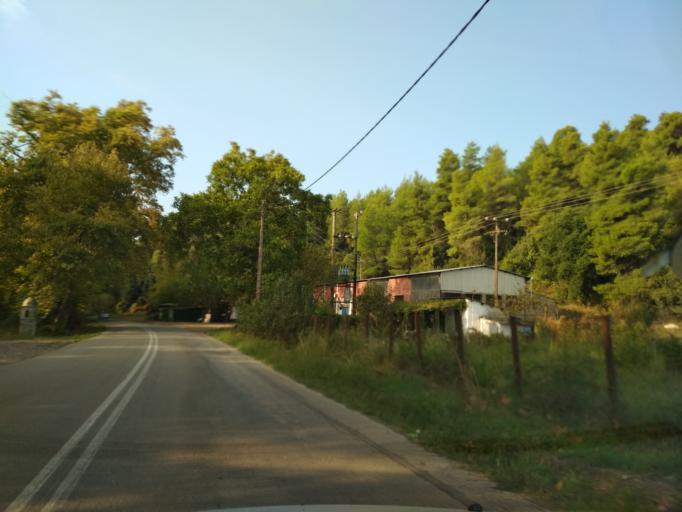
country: GR
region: Central Greece
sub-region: Nomos Evvoias
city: Mantoudi
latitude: 38.7872
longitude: 23.4710
